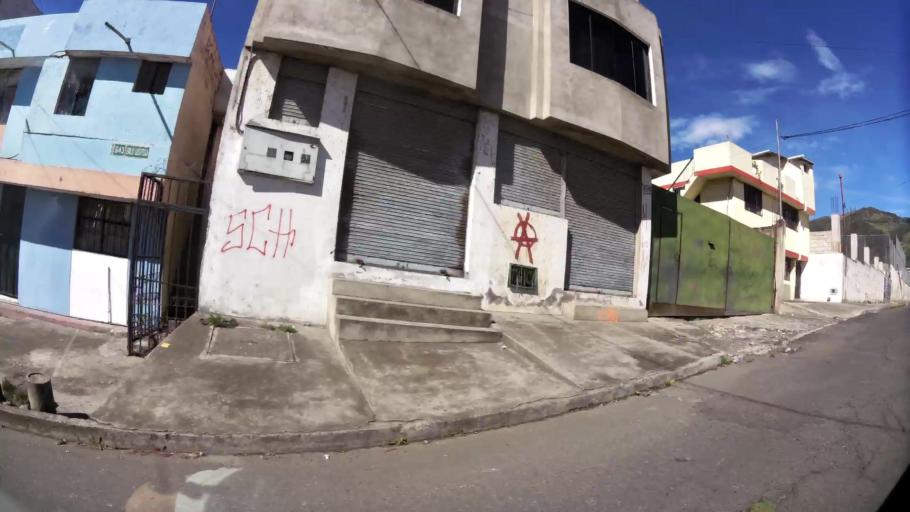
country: EC
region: Pichincha
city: Quito
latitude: -0.3041
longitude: -78.5628
